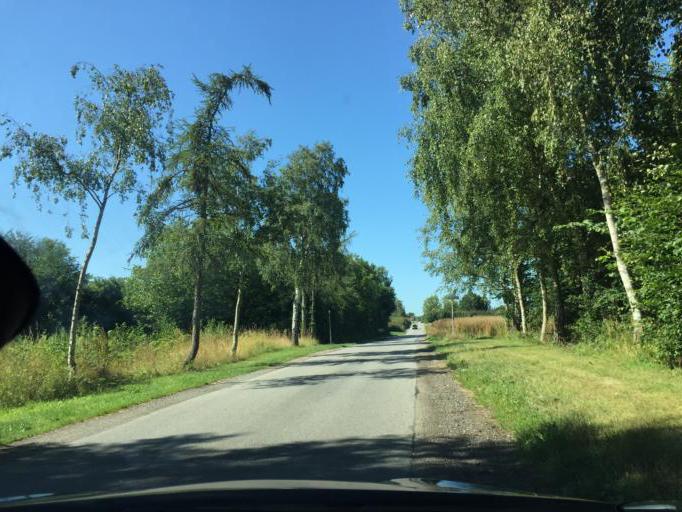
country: DK
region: South Denmark
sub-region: Nordfyns Kommune
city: Sonderso
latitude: 55.4787
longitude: 10.2675
